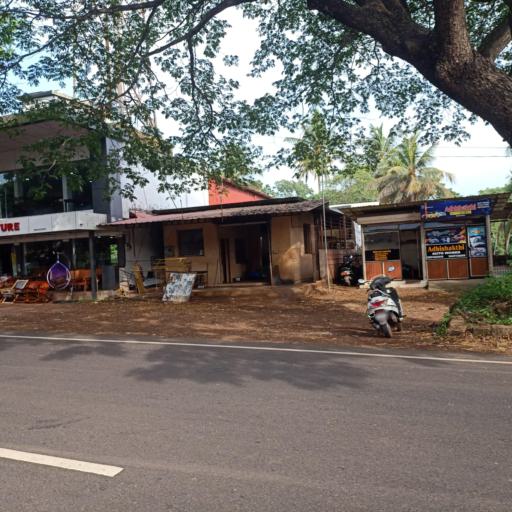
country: IN
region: Kerala
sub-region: Kasaragod District
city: Kasaragod
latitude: 12.5083
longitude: 75.0976
